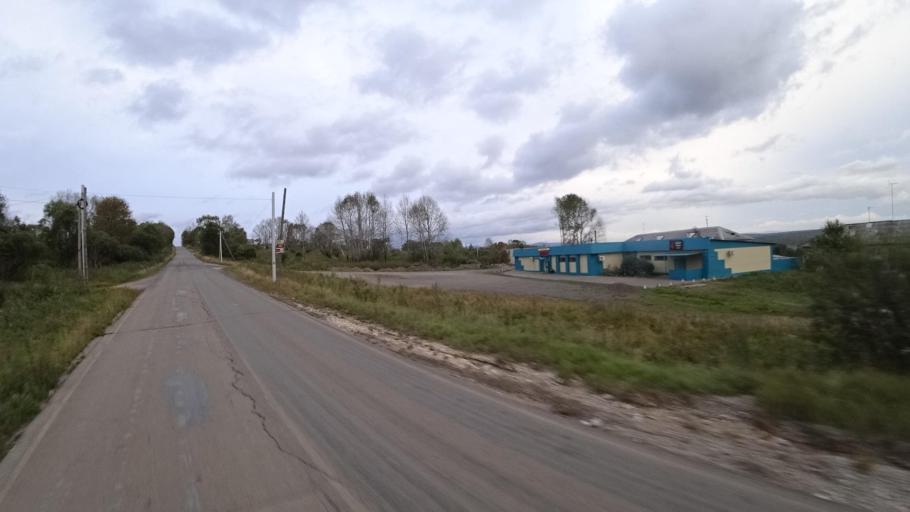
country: RU
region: Jewish Autonomous Oblast
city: Izvestkovyy
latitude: 48.9736
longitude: 131.5788
